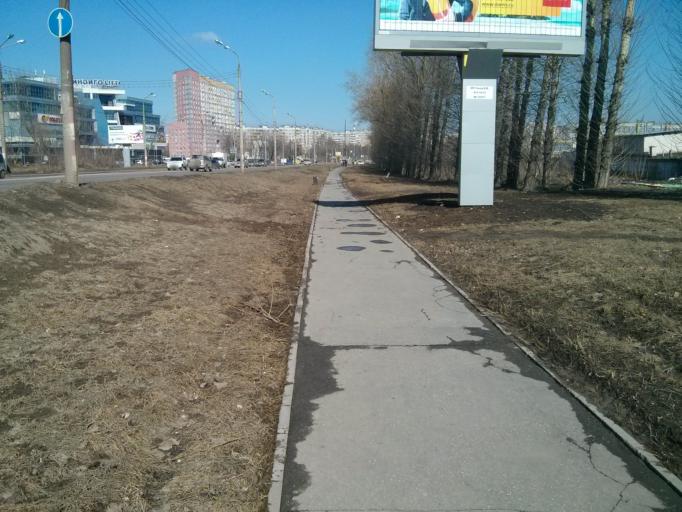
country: RU
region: Nizjnij Novgorod
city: Afonino
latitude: 56.2882
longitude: 44.0763
